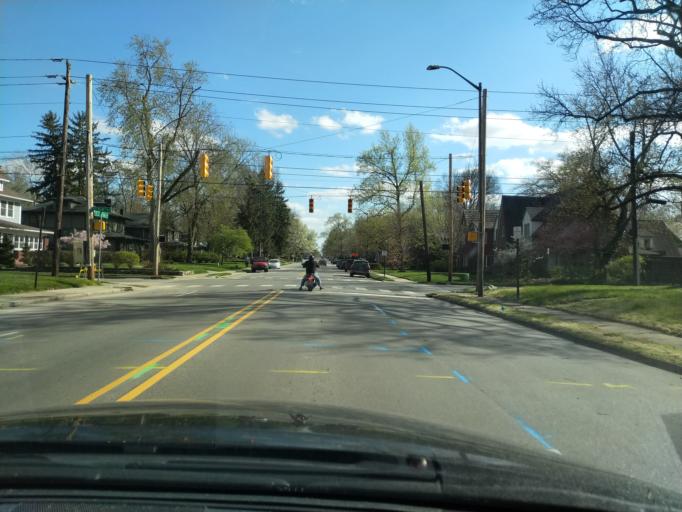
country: US
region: Indiana
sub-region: Marion County
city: Broad Ripple
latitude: 39.8513
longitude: -86.1501
